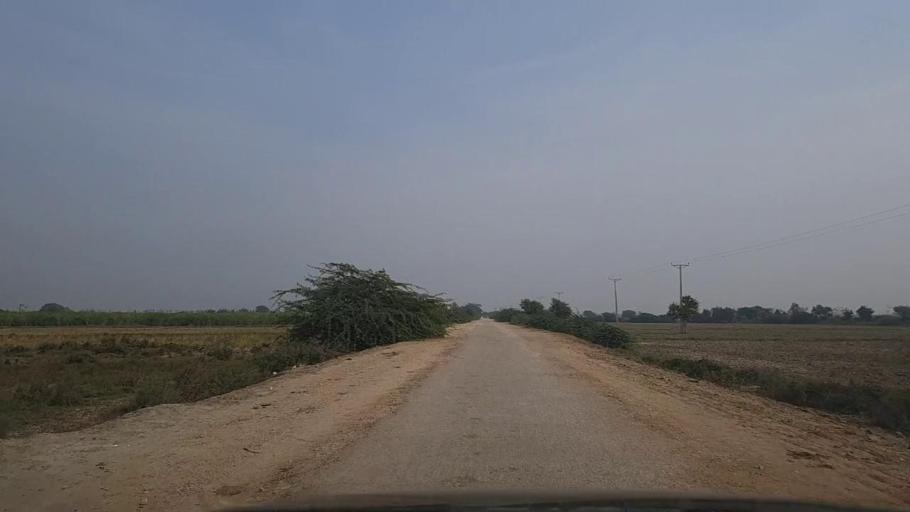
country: PK
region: Sindh
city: Mirpur Sakro
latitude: 24.4026
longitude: 67.7444
